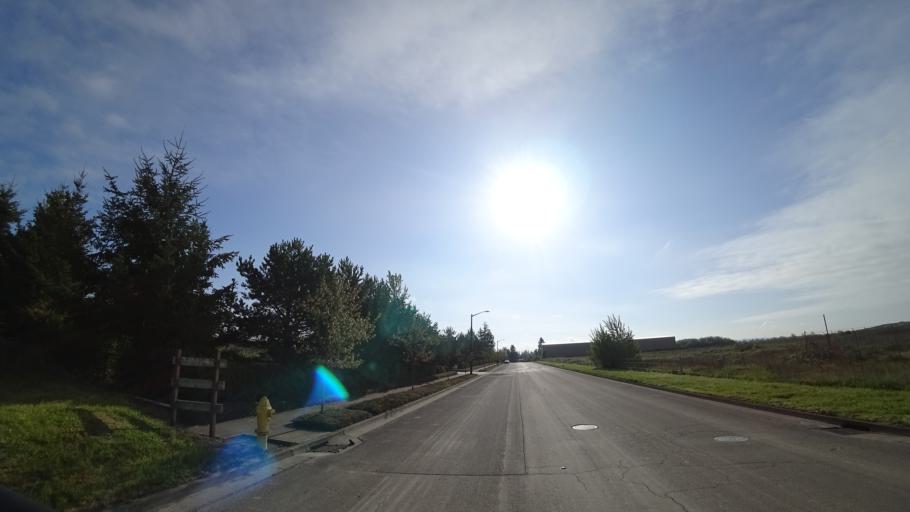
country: US
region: Oregon
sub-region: Washington County
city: Hillsboro
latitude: 45.5126
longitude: -122.9998
